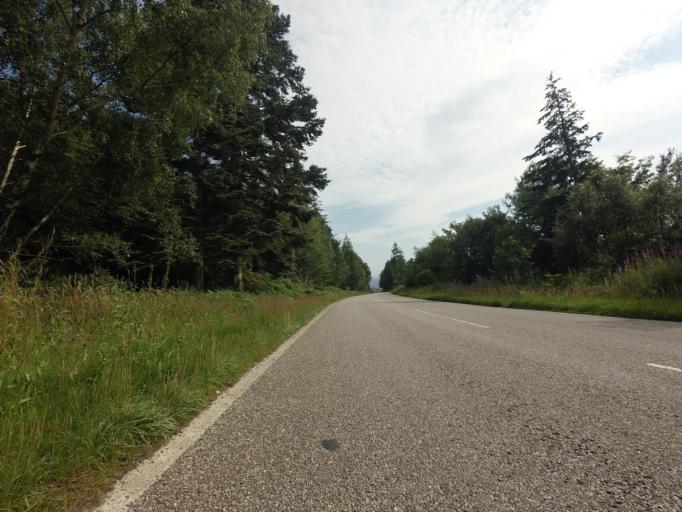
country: GB
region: Scotland
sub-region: Highland
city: Alness
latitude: 57.9069
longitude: -4.3612
